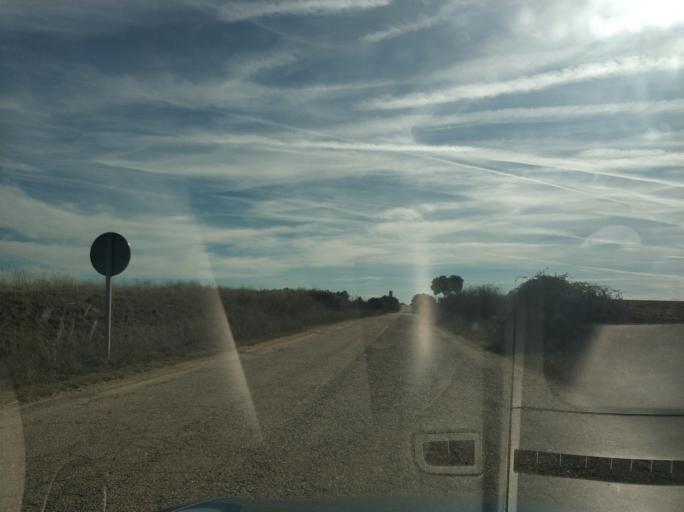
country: ES
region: Castille and Leon
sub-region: Provincia de Zamora
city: Cuelgamures
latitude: 41.2512
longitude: -5.7089
